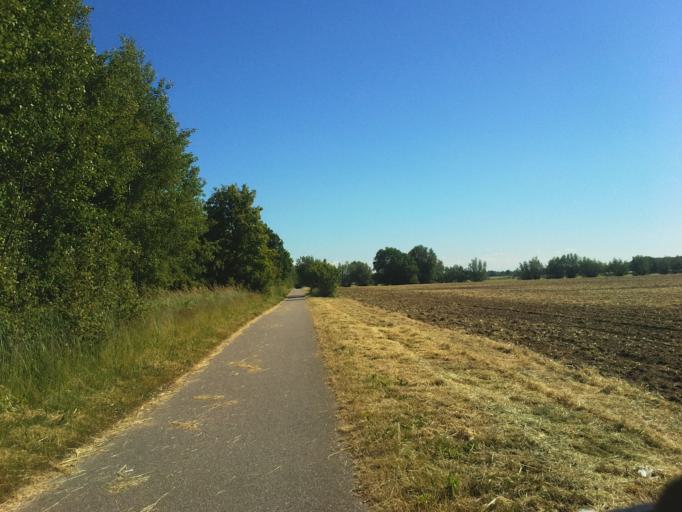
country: DE
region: Mecklenburg-Vorpommern
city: Nienhagen
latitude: 54.1578
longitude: 12.1756
